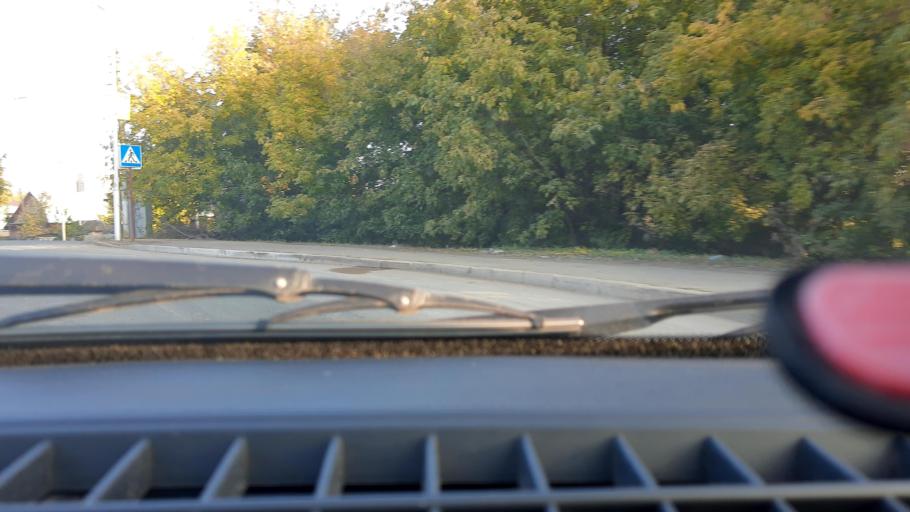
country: RU
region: Bashkortostan
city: Ufa
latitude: 54.7181
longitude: 55.9684
